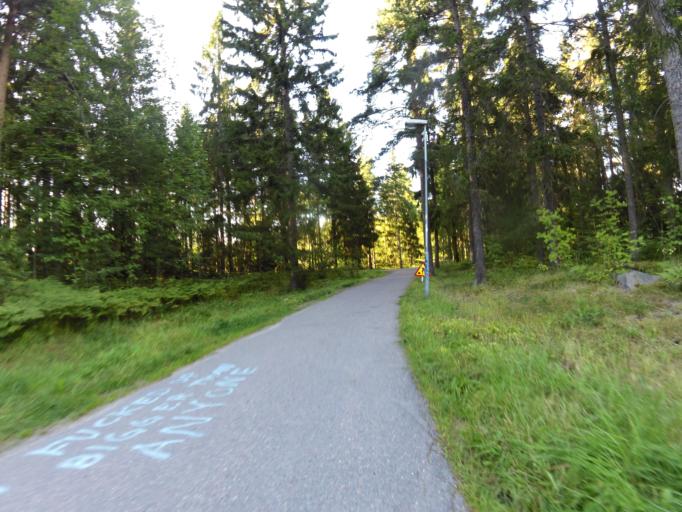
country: SE
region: Gaevleborg
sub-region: Gavle Kommun
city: Gavle
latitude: 60.6557
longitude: 17.1506
